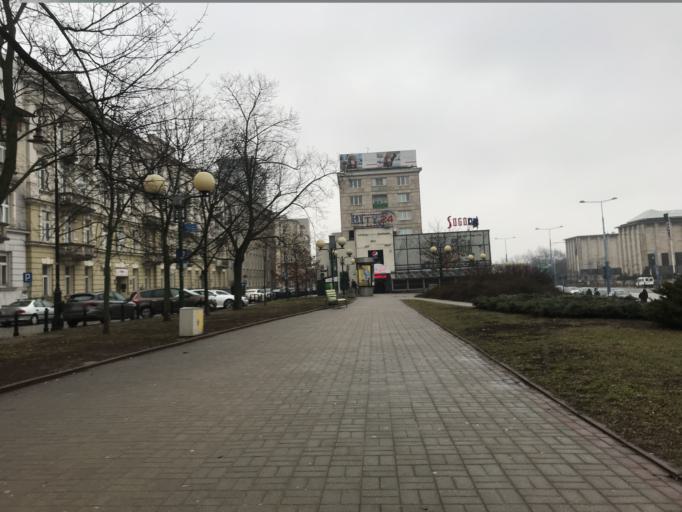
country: PL
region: Masovian Voivodeship
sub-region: Warszawa
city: Srodmiescie
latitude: 52.2324
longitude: 21.0218
